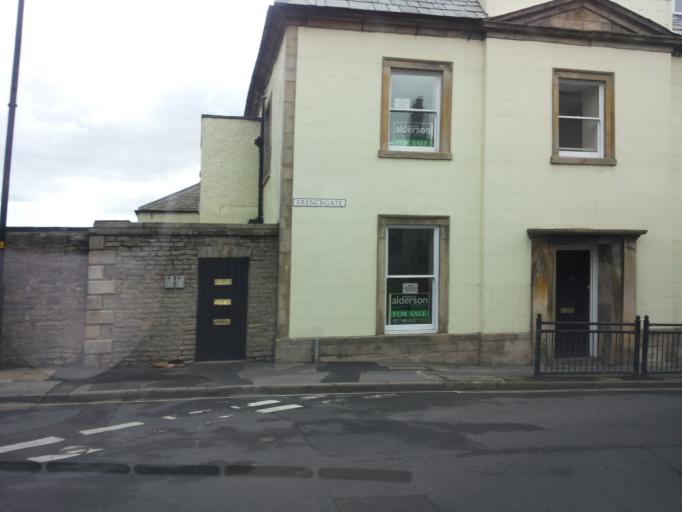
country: GB
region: England
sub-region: North Yorkshire
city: Catterick Garrison
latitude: 54.4047
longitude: -1.7346
